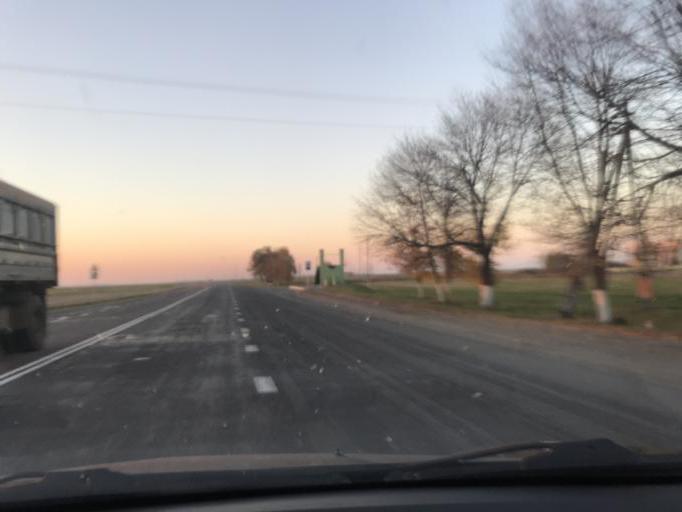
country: BY
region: Gomel
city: Loyew
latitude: 52.1449
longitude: 30.6070
